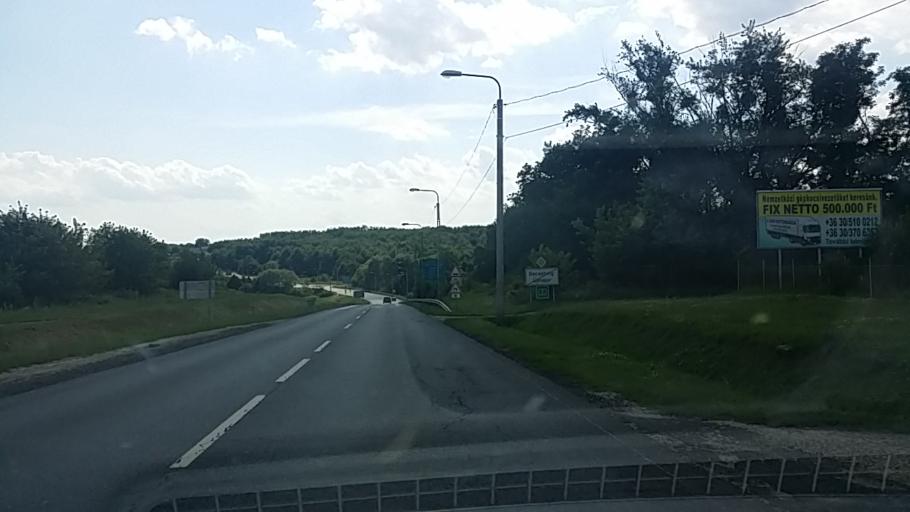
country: HU
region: Zala
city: Becsehely
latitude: 46.4543
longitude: 16.8176
